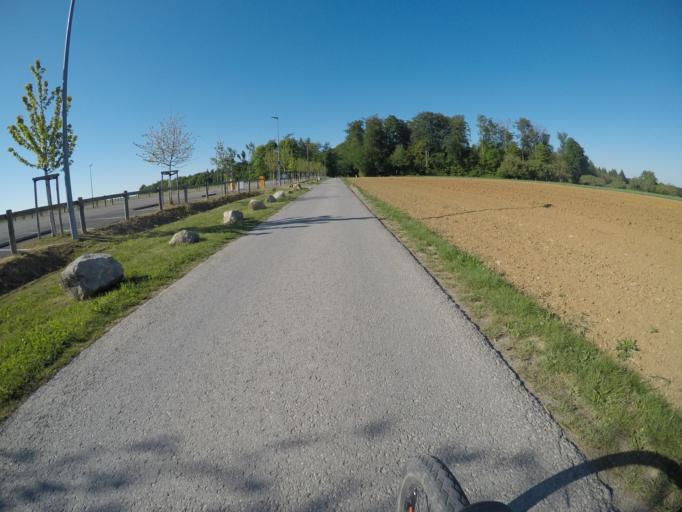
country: DE
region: Baden-Wuerttemberg
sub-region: Regierungsbezirk Stuttgart
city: Weissach
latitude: 48.8549
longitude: 8.8989
